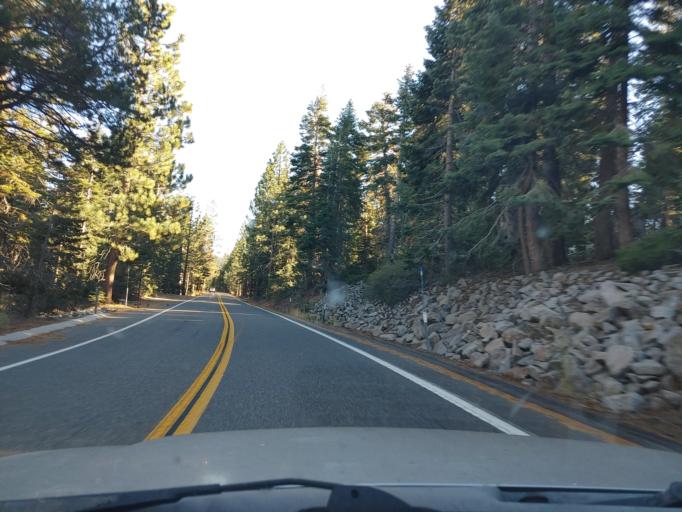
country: US
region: California
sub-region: Placer County
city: Tahoma
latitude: 39.0069
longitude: -120.1173
